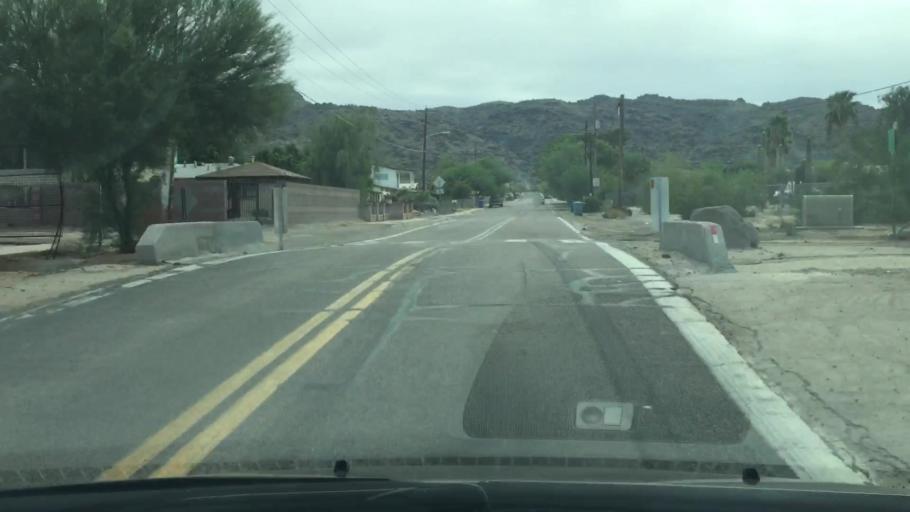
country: US
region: Arizona
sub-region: Maricopa County
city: Guadalupe
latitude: 33.3740
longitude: -112.0316
